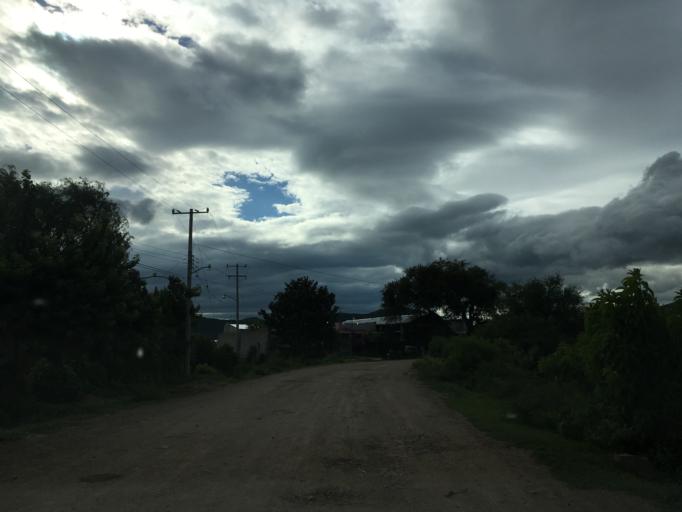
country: MX
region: Guanajuato
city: Iramuco
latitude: 19.9685
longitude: -100.9474
